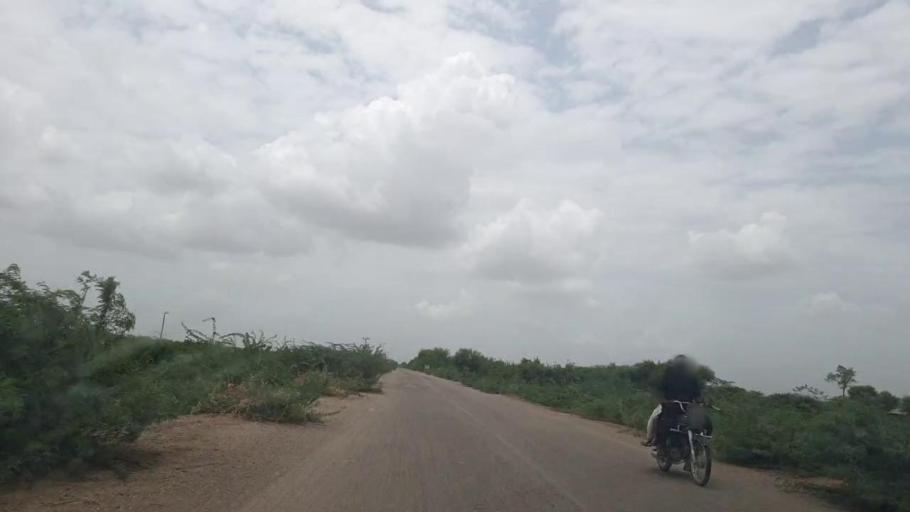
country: PK
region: Sindh
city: Naukot
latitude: 24.9292
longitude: 69.2759
